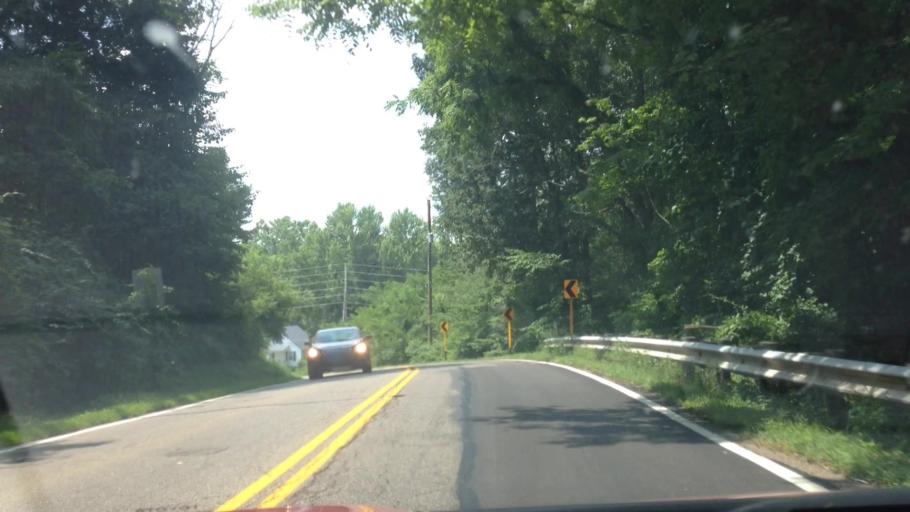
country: US
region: Ohio
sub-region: Stark County
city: Massillon
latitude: 40.8598
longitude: -81.5200
